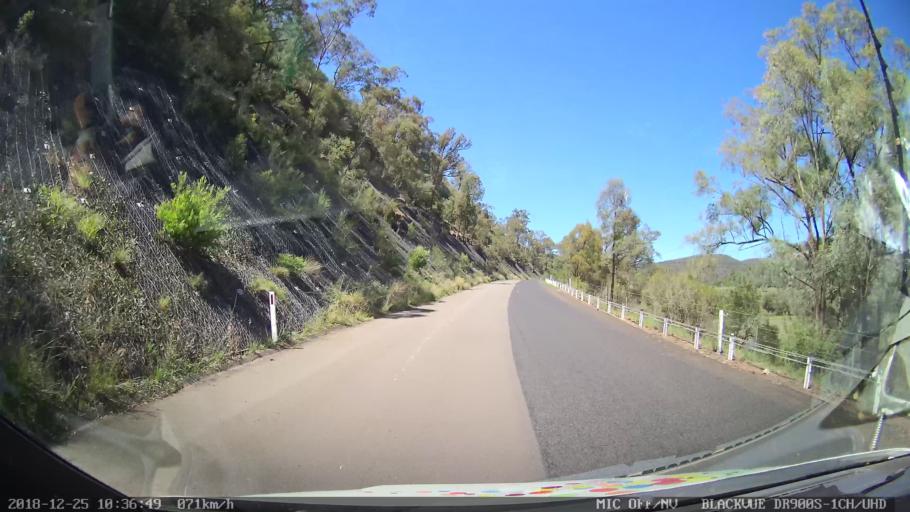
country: AU
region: New South Wales
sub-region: Upper Hunter Shire
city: Merriwa
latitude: -32.4077
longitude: 150.3832
